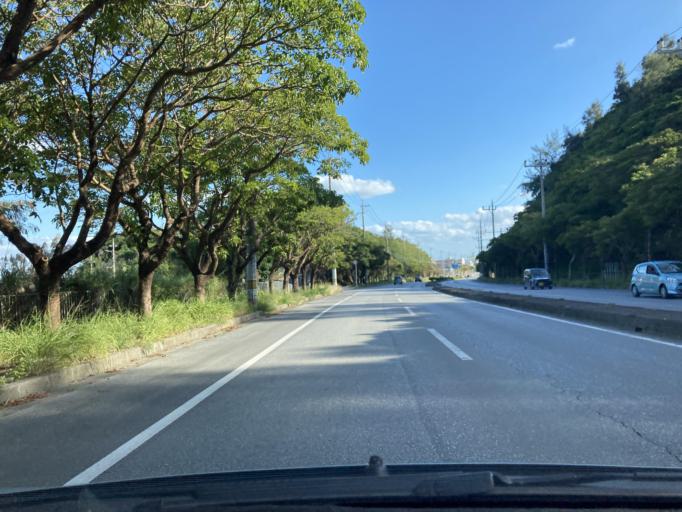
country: JP
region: Okinawa
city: Gushikawa
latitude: 26.3429
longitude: 127.8419
